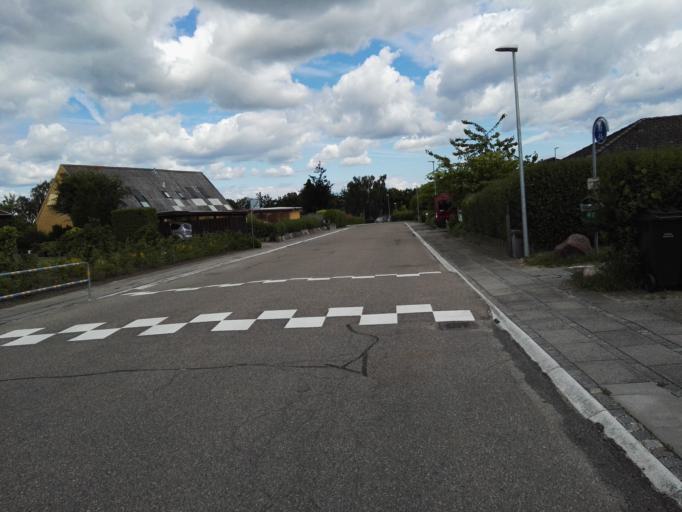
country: DK
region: Capital Region
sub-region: Egedal Kommune
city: Stenlose
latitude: 55.7708
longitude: 12.1856
